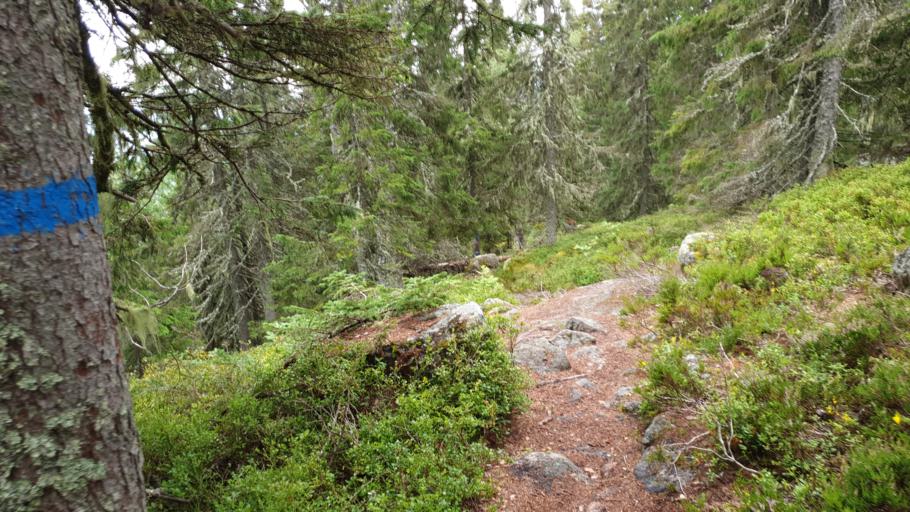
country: SE
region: Gaevleborg
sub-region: Hudiksvalls Kommun
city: Sorforsa
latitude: 61.6416
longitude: 16.7665
